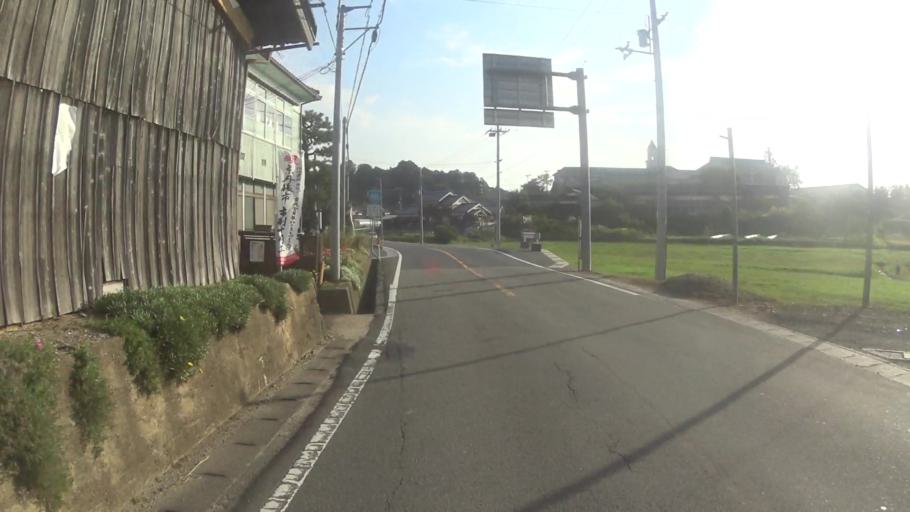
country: JP
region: Kyoto
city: Miyazu
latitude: 35.6799
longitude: 135.0987
